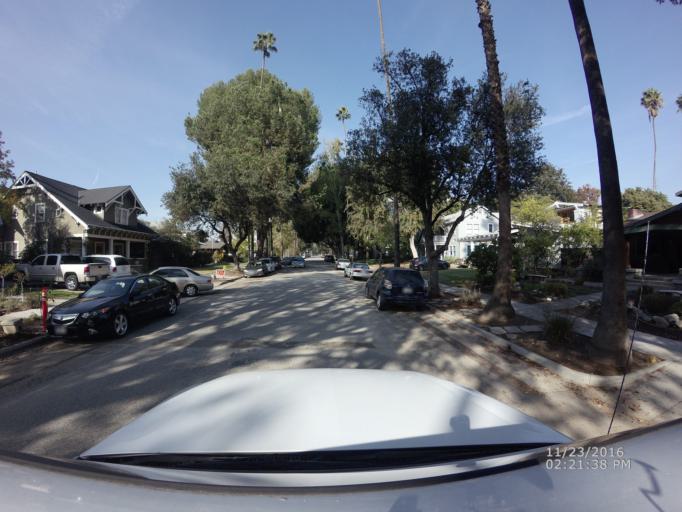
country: US
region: California
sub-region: Los Angeles County
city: South Pasadena
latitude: 34.1016
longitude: -118.1425
